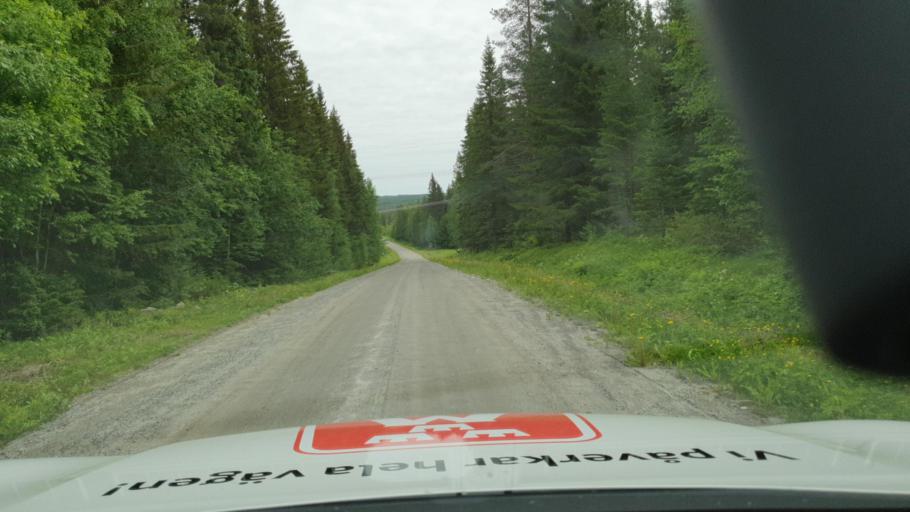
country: SE
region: Vaesterbotten
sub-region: Skelleftea Kommun
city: Langsele
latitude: 64.5091
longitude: 20.2858
